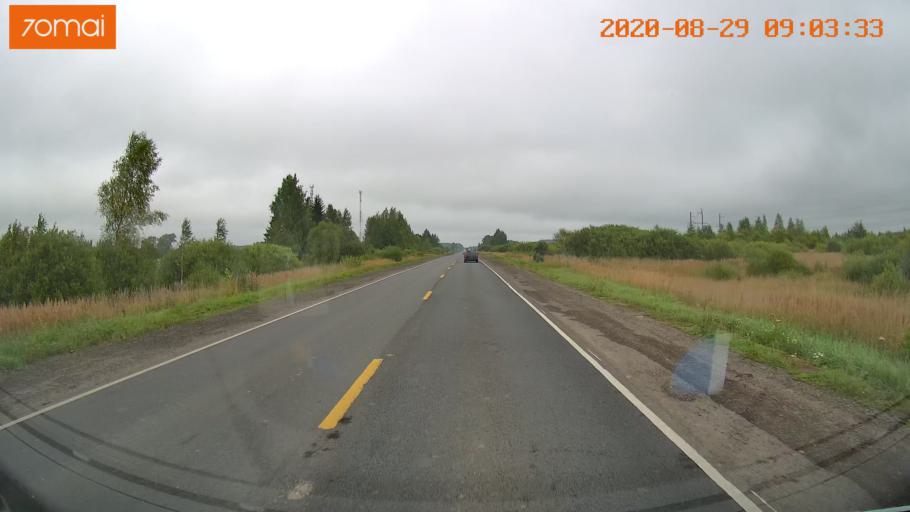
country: RU
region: Ivanovo
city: Staraya Vichuga
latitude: 57.3388
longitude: 41.9692
